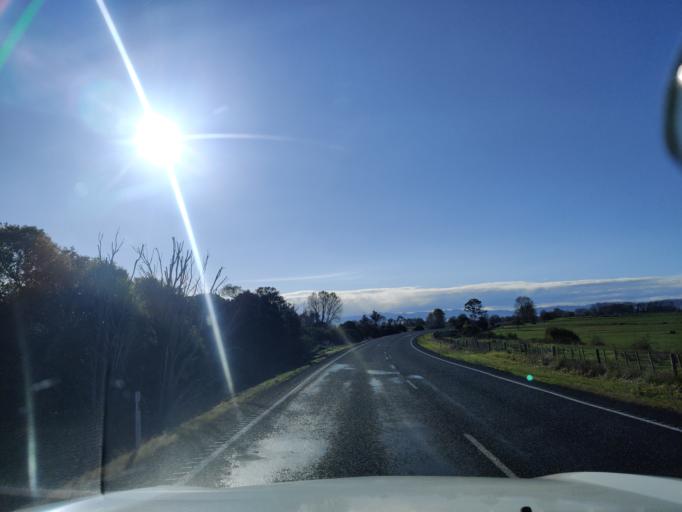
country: NZ
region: Waikato
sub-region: Hauraki District
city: Ngatea
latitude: -37.2820
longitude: 175.4023
